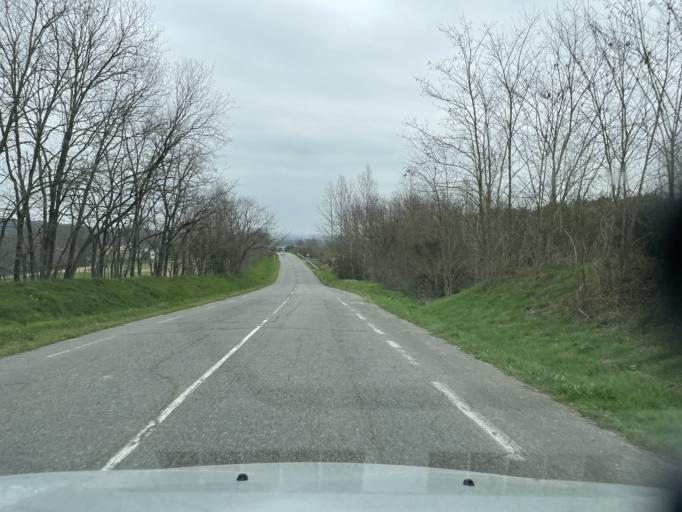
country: FR
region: Midi-Pyrenees
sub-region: Departement du Gers
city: Pujaudran
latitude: 43.5892
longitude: 1.1629
